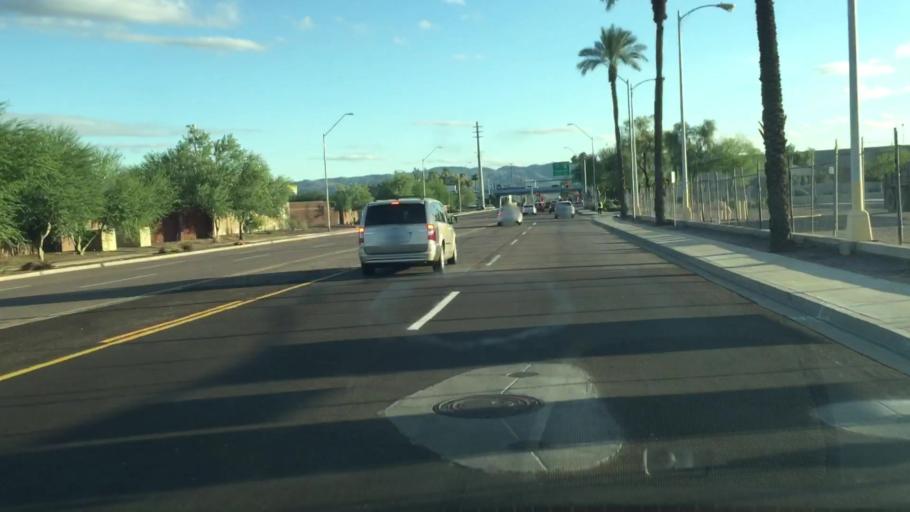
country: US
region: Arizona
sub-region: Maricopa County
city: Phoenix
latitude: 33.4304
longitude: -112.0479
